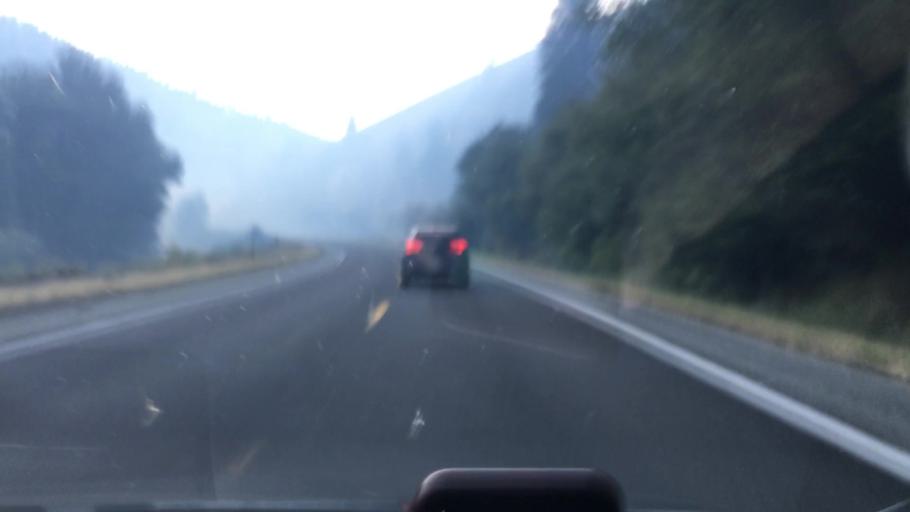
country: US
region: Idaho
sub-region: Valley County
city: McCall
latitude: 45.2818
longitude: -116.3467
